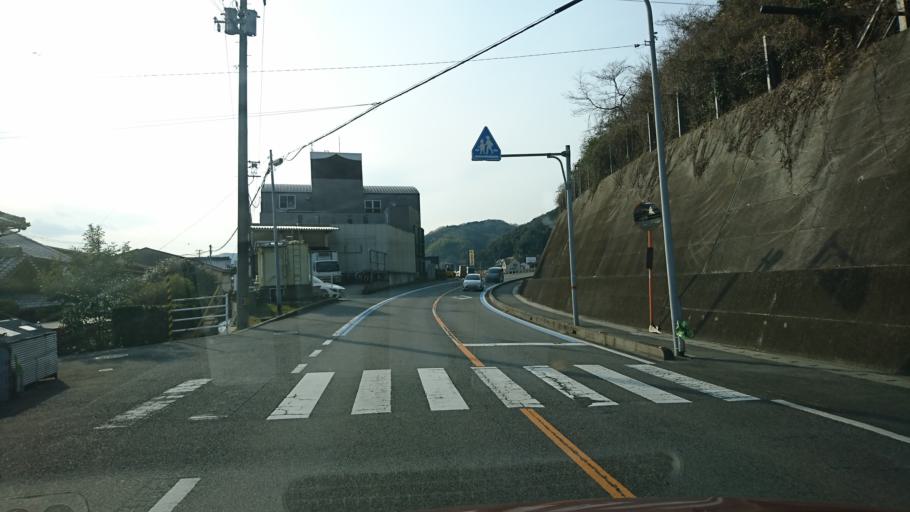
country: JP
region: Ehime
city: Hojo
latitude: 34.0274
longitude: 132.9578
